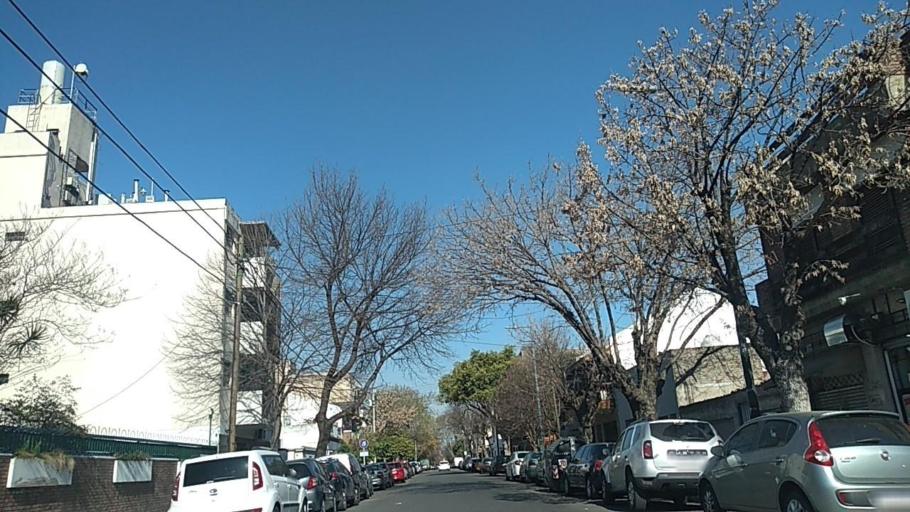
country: AR
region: Buenos Aires F.D.
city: Villa Santa Rita
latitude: -34.6041
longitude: -58.5045
